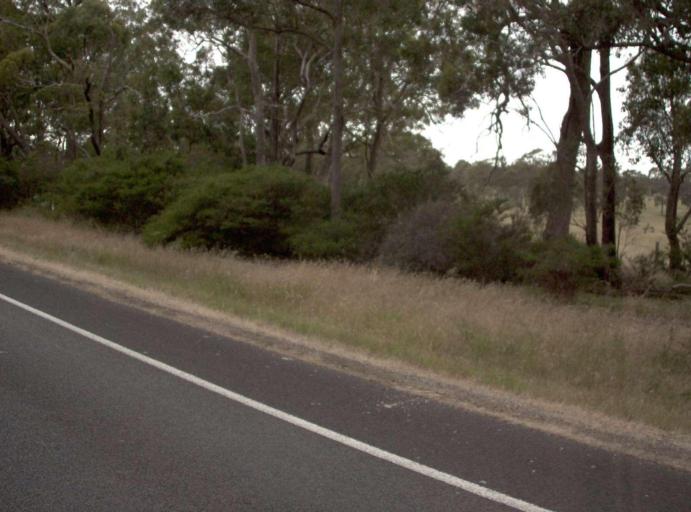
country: AU
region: Victoria
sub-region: Wellington
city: Sale
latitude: -38.4488
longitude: 146.9417
